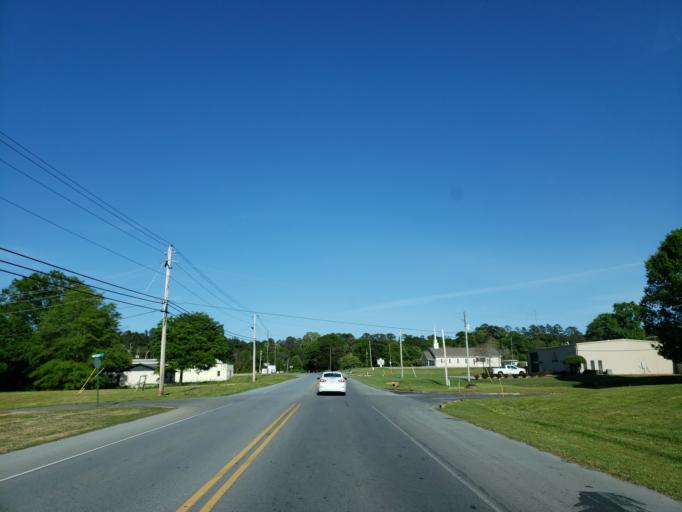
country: US
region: Georgia
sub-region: Polk County
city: Cedartown
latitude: 34.0141
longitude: -85.2318
